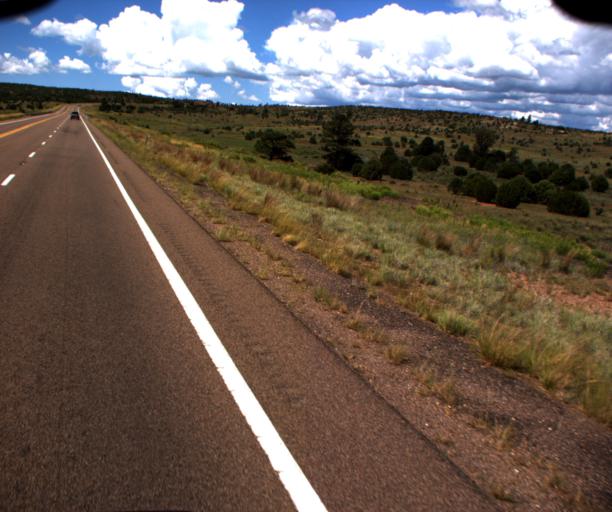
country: US
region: Arizona
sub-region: Navajo County
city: Heber-Overgaard
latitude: 34.3672
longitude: -110.4094
